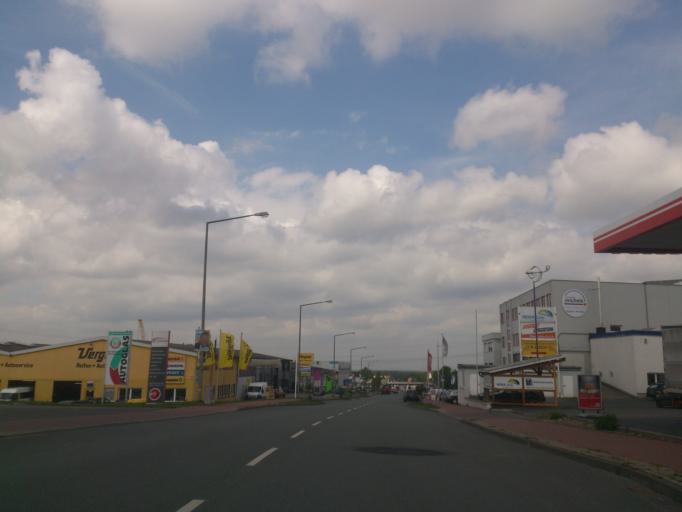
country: DE
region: North Rhine-Westphalia
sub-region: Regierungsbezirk Detmold
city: Paderborn
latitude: 51.6977
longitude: 8.7322
